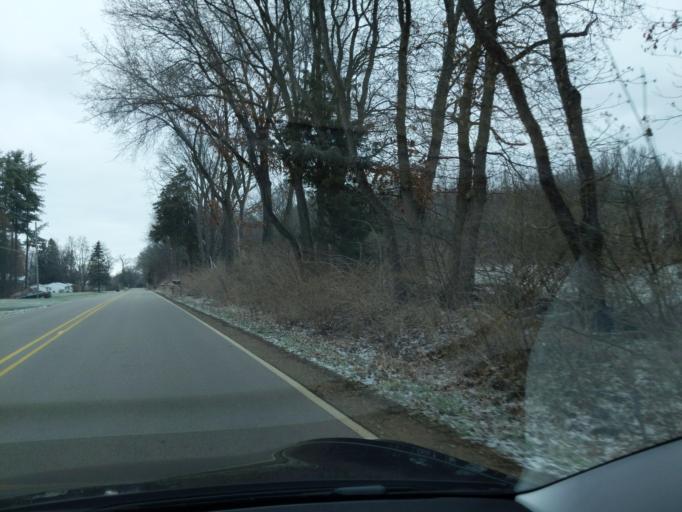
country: US
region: Michigan
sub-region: Jackson County
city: Spring Arbor
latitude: 42.2231
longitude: -84.5167
